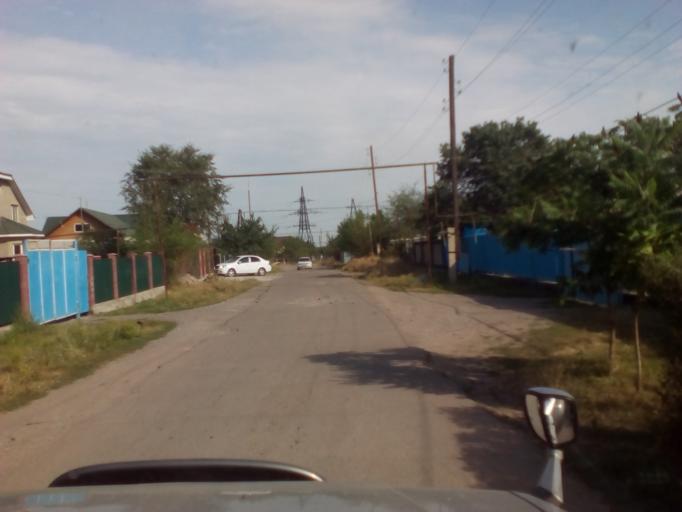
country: KZ
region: Almaty Oblysy
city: Burunday
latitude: 43.1682
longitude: 76.4032
